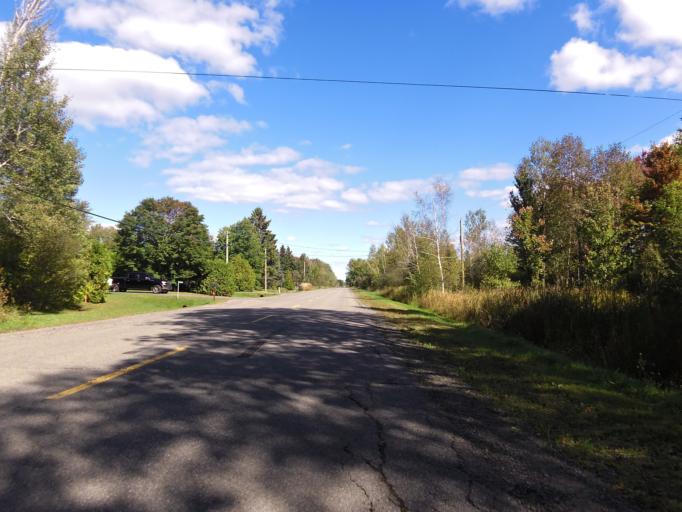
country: CA
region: Ontario
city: Ottawa
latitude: 45.3407
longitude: -75.4767
